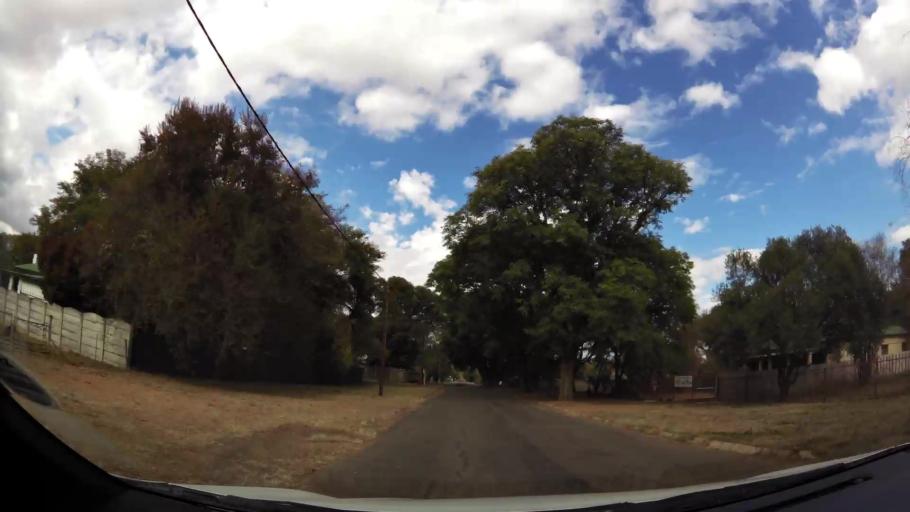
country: ZA
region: Limpopo
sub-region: Waterberg District Municipality
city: Modimolle
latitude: -24.7072
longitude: 28.4021
